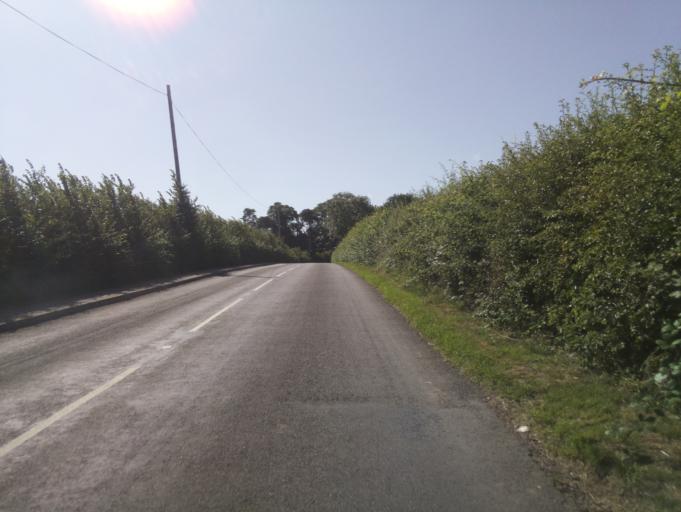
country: GB
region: England
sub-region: Milton Keynes
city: Calverton
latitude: 52.0015
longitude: -0.8657
